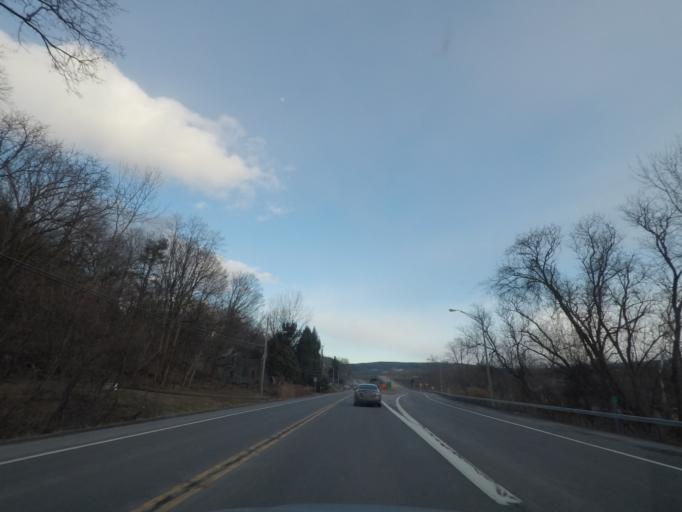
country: US
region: New York
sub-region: Herkimer County
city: Ilion
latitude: 43.0238
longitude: -75.0335
